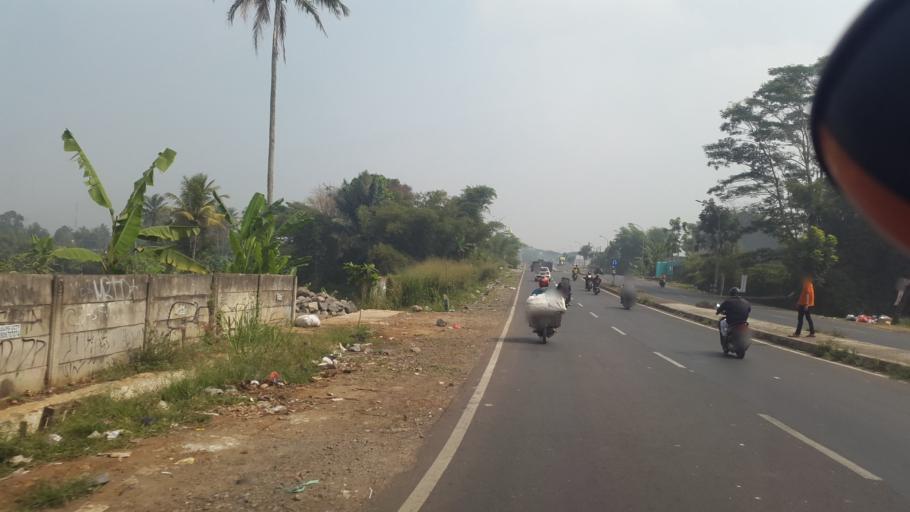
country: ID
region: West Java
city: Sukabumi
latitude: -6.9157
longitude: 106.8828
